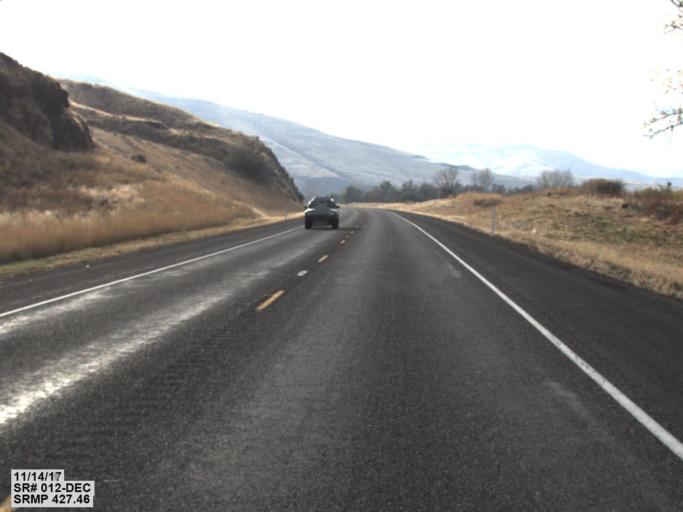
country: US
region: Washington
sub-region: Asotin County
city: Clarkston Heights-Vineland
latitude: 46.4215
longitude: -117.1693
